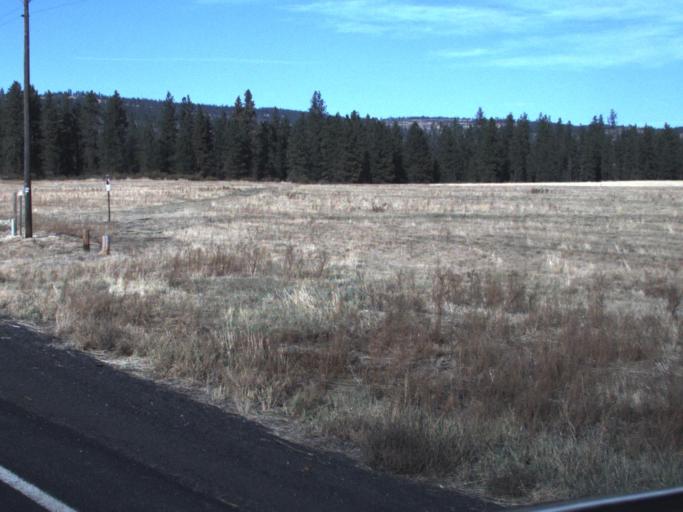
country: US
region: Washington
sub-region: Lincoln County
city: Davenport
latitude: 47.9051
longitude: -118.3049
